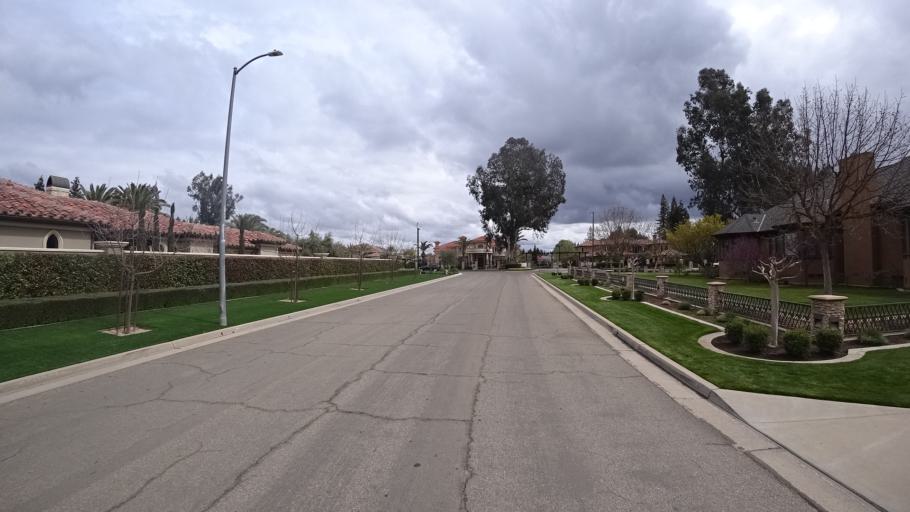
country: US
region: California
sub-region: Fresno County
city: Fresno
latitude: 36.8473
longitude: -119.8361
